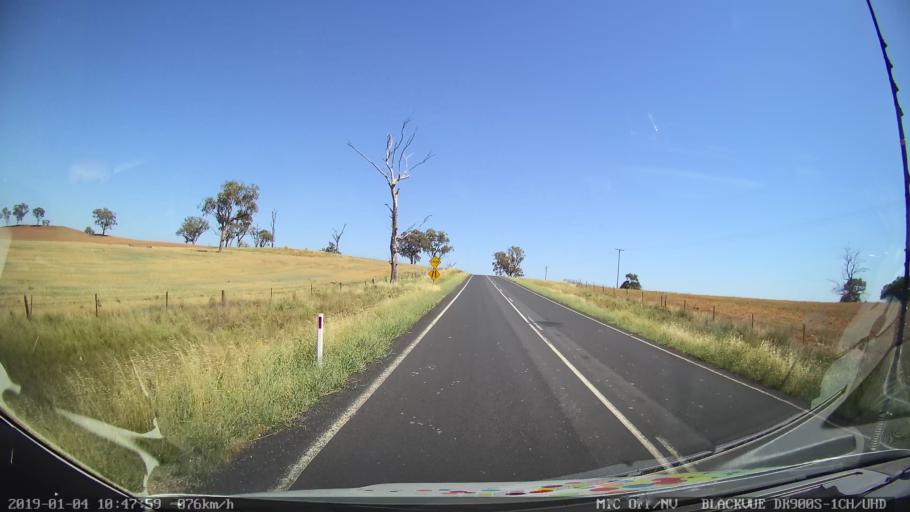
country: AU
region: New South Wales
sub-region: Cabonne
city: Molong
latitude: -33.2645
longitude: 148.7159
